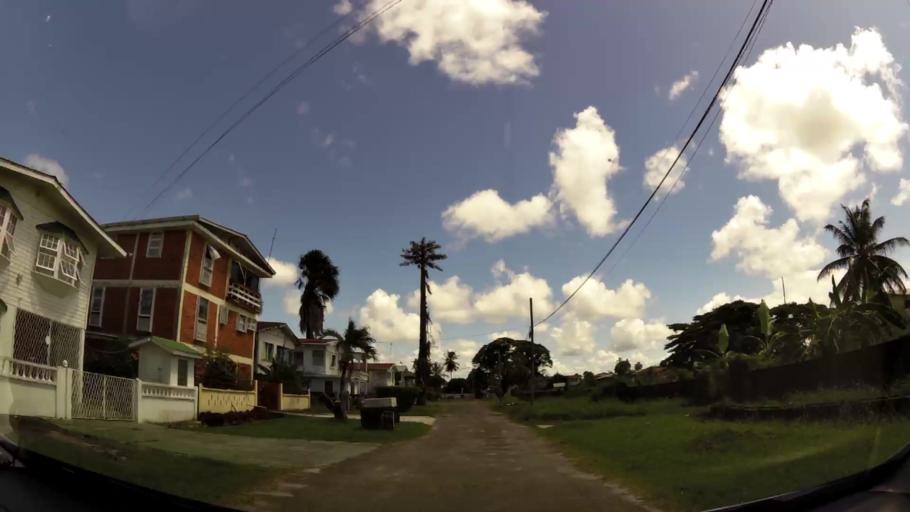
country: GY
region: Demerara-Mahaica
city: Georgetown
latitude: 6.7979
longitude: -58.1358
